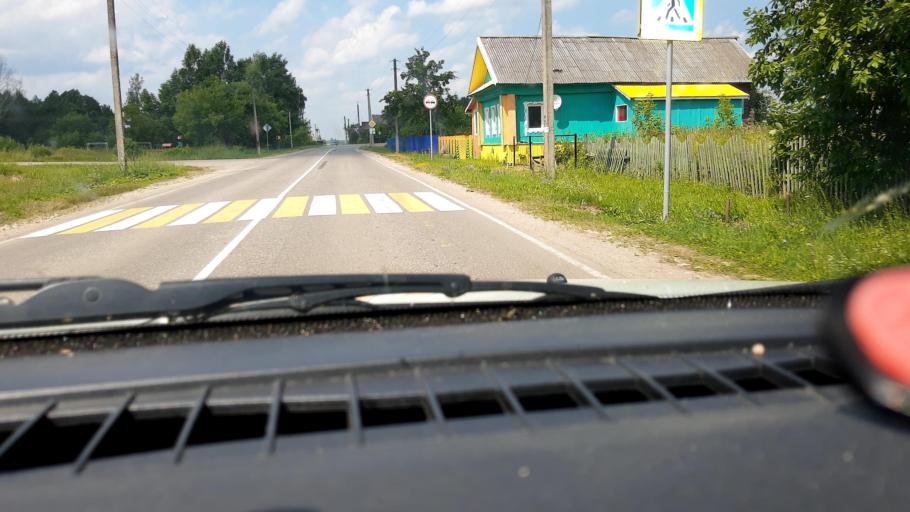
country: RU
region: Nizjnij Novgorod
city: Sharanga
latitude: 57.1282
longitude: 46.5110
